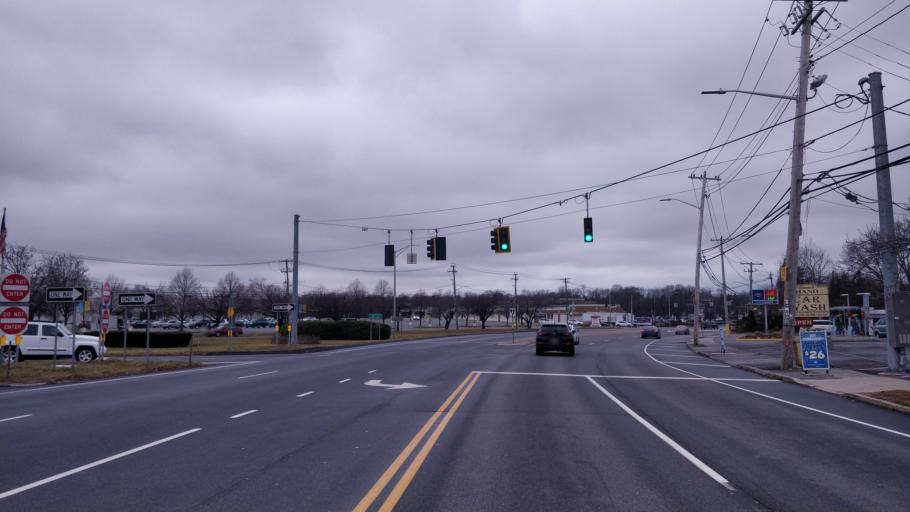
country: US
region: New York
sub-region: Suffolk County
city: Commack
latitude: 40.8425
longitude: -73.2881
